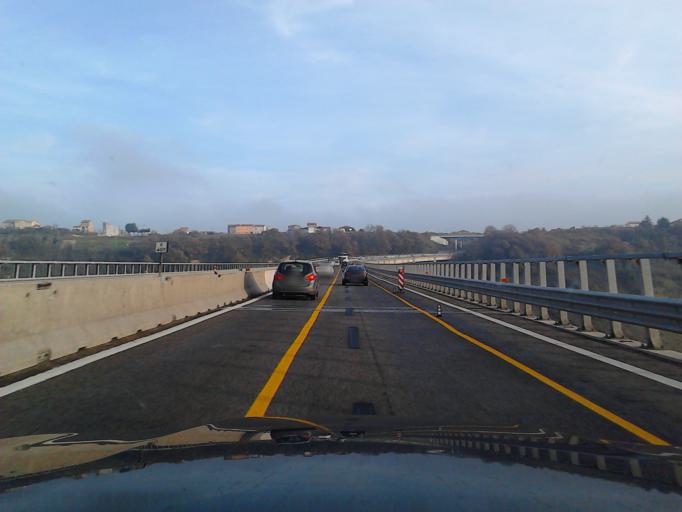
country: IT
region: Abruzzo
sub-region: Provincia di Chieti
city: Marina di San Vito
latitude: 42.3130
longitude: 14.4147
